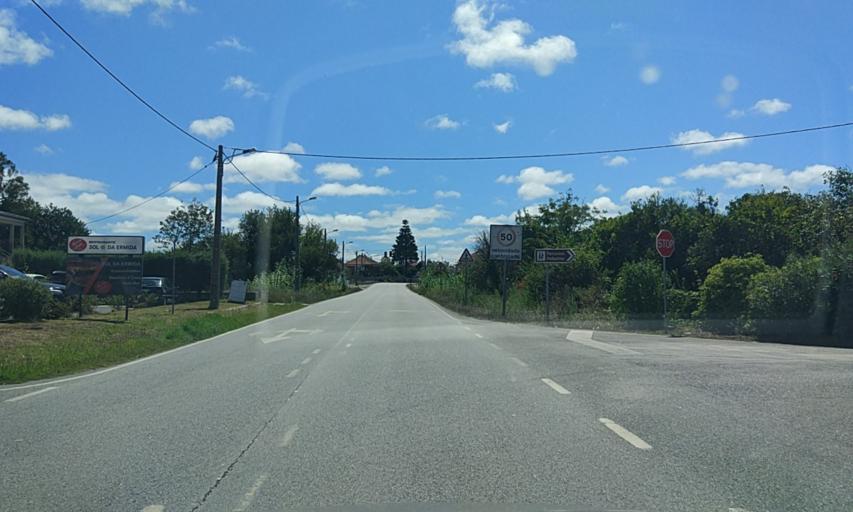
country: PT
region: Coimbra
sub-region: Mira
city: Mira
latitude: 40.4005
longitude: -8.7356
